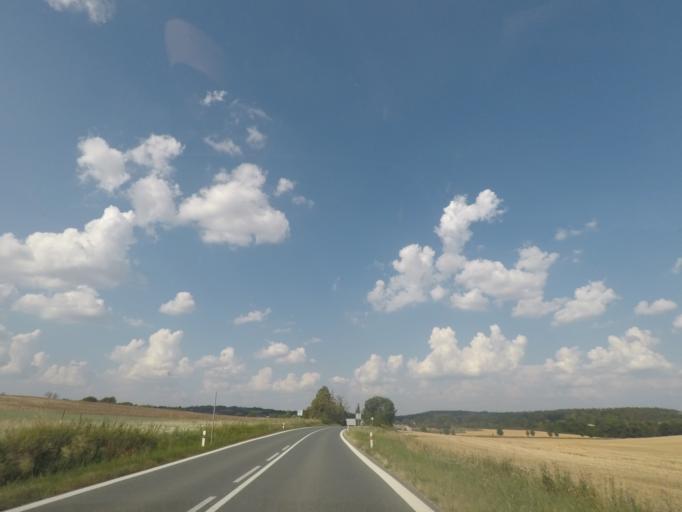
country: CZ
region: Kralovehradecky
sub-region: Okres Nachod
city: Jaromer
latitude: 50.3746
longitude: 15.9139
